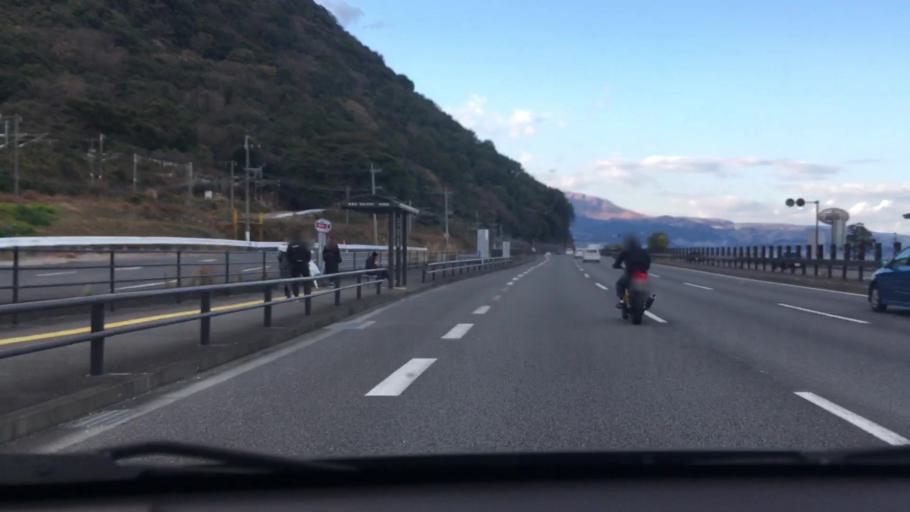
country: JP
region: Oita
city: Beppu
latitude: 33.2591
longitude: 131.5333
